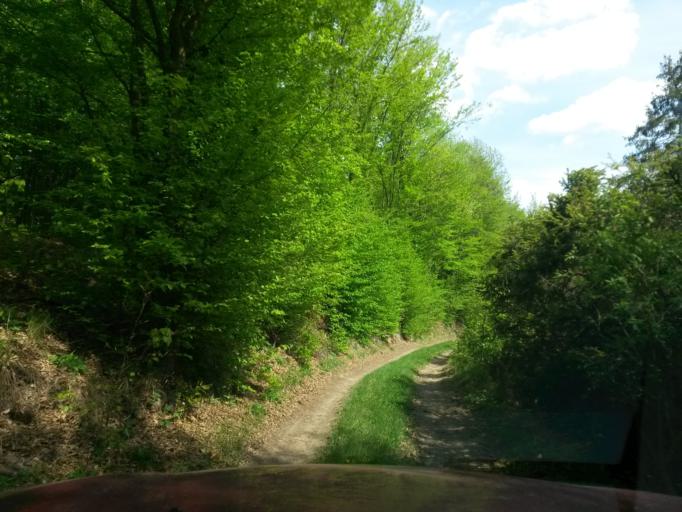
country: SK
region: Kosicky
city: Gelnica
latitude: 48.8328
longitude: 21.0670
